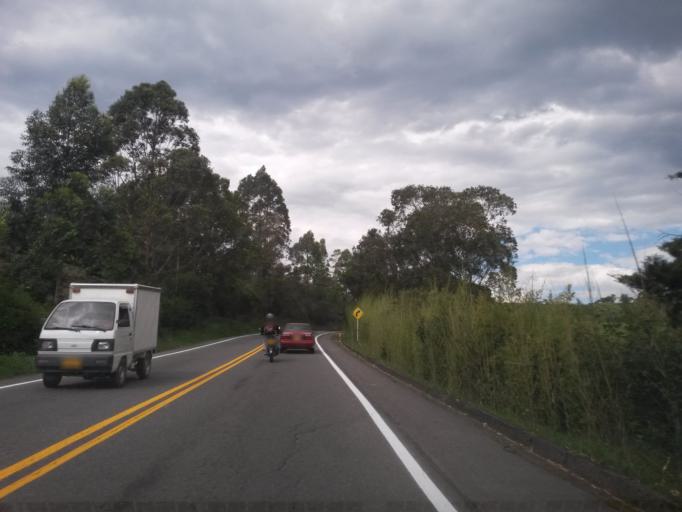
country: CO
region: Cauca
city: Popayan
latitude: 2.3672
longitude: -76.6807
